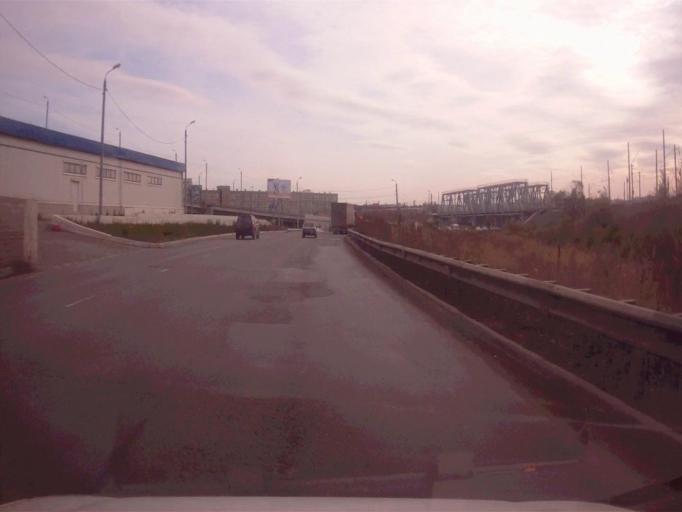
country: RU
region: Chelyabinsk
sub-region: Gorod Chelyabinsk
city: Chelyabinsk
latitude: 55.1569
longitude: 61.4413
